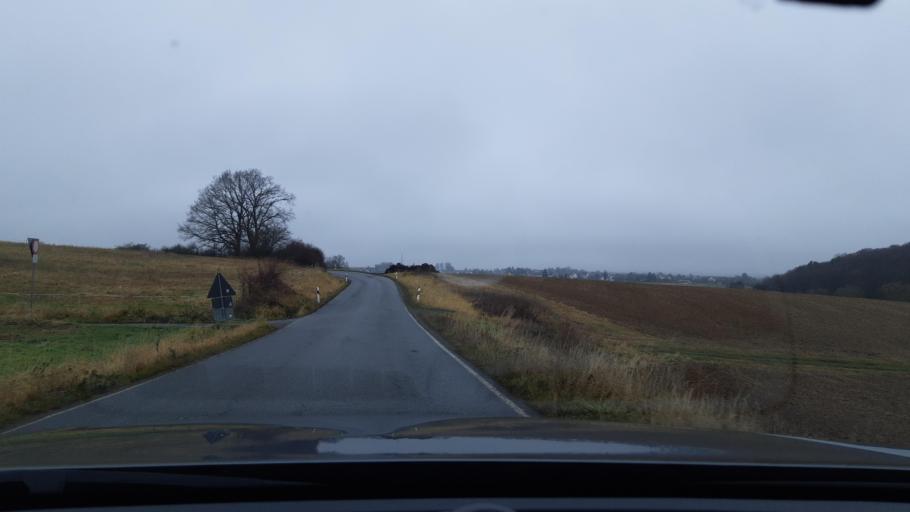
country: DE
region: Hesse
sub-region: Regierungsbezirk Giessen
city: Schoeffengrund
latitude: 50.4953
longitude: 8.5492
